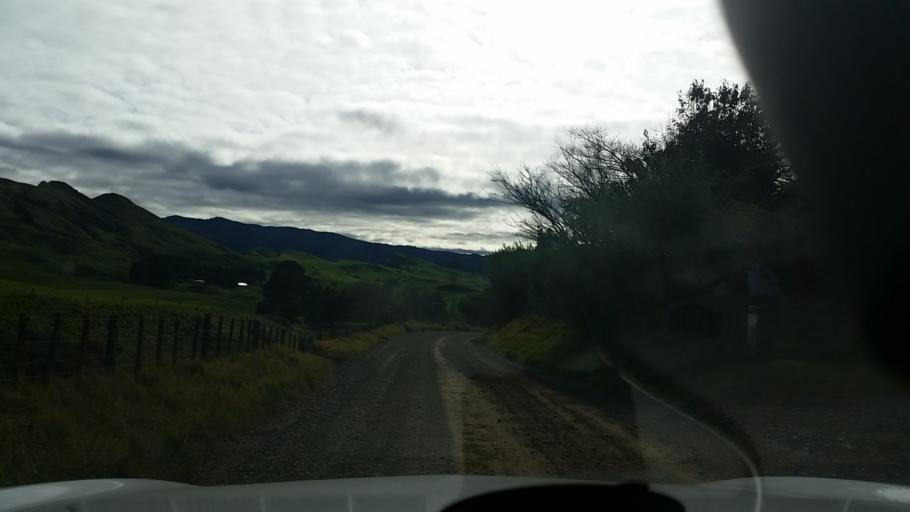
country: NZ
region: Hawke's Bay
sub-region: Napier City
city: Napier
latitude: -39.1316
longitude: 176.8959
